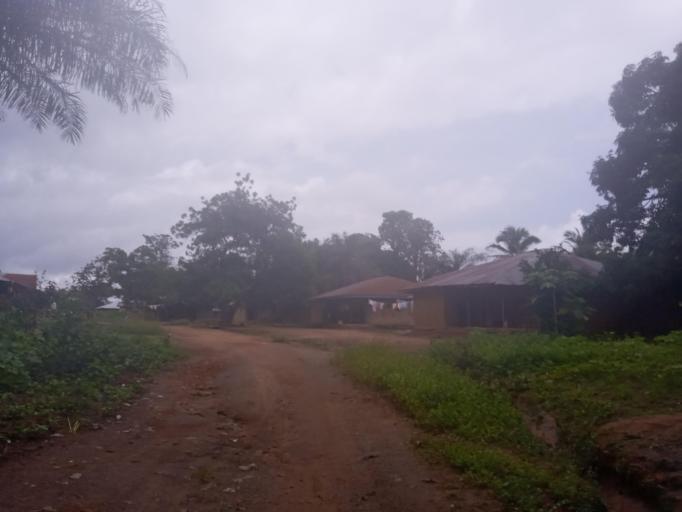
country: SL
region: Northern Province
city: Bumbuna
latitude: 8.9532
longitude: -11.7594
